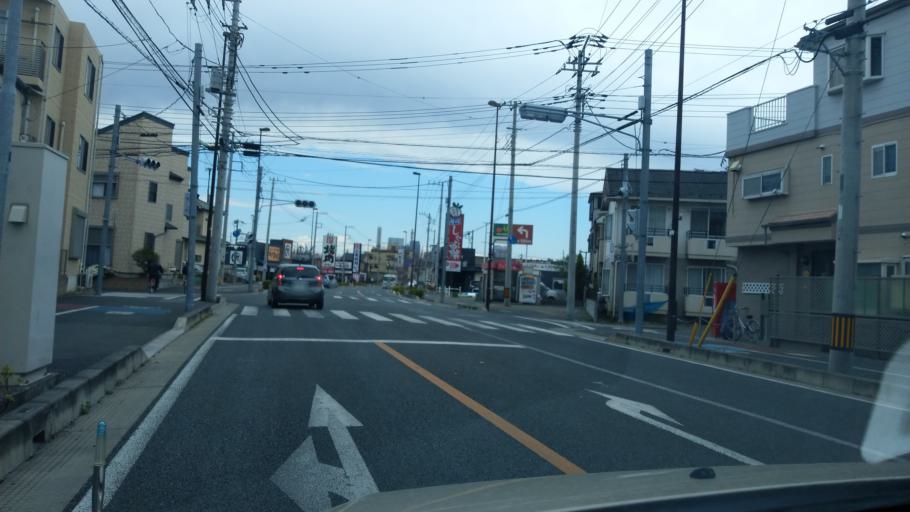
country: JP
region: Saitama
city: Yono
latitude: 35.8680
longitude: 139.6329
